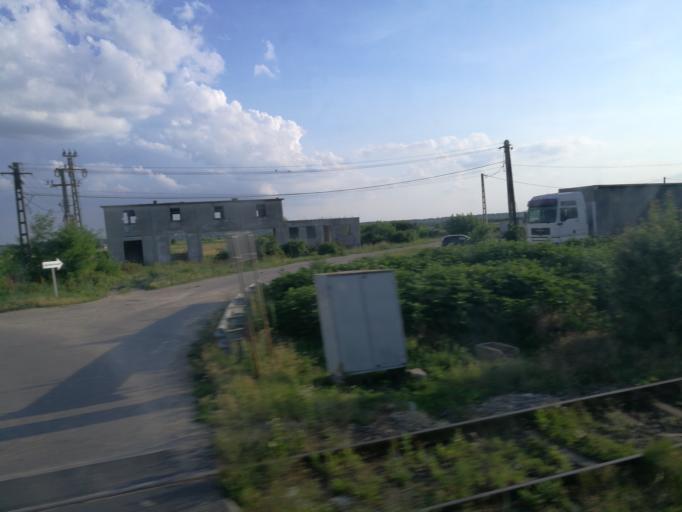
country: RO
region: Arges
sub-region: Comuna Calinesti
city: Calinesti
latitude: 44.8088
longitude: 25.0665
